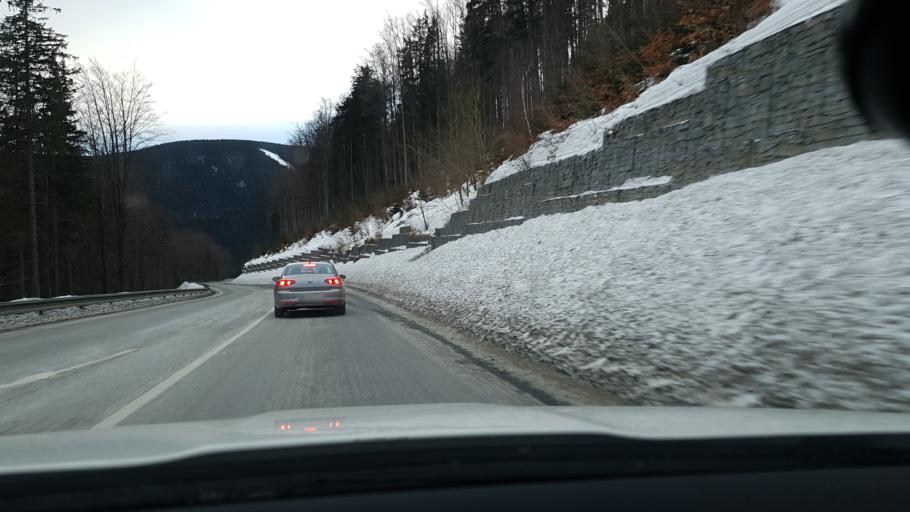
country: CZ
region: Olomoucky
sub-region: Okres Jesenik
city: Jesenik
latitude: 50.1419
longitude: 17.1620
